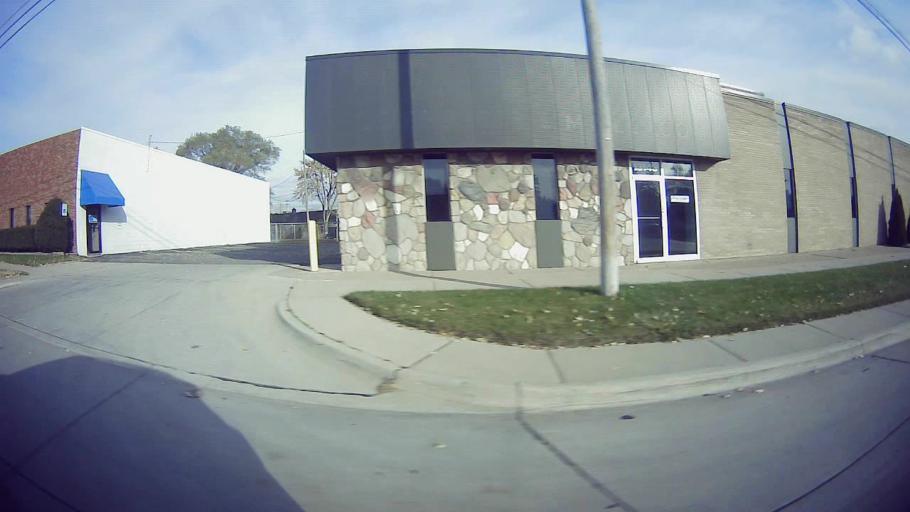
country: US
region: Michigan
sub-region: Macomb County
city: Eastpointe
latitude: 42.4638
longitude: -82.9912
